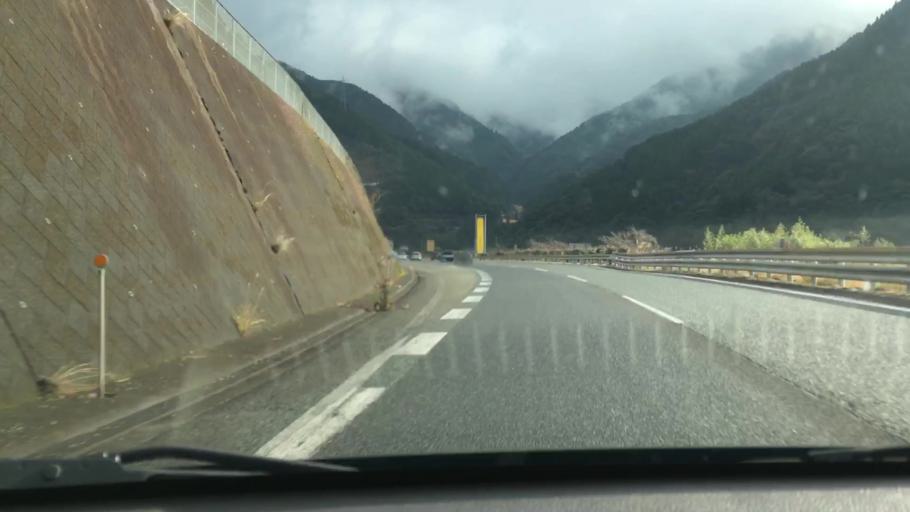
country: JP
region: Kumamoto
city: Yatsushiro
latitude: 32.3981
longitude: 130.7029
